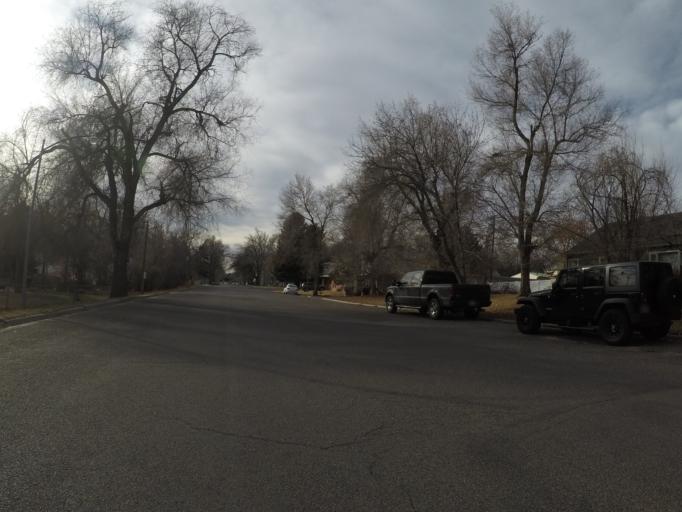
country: US
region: Montana
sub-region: Yellowstone County
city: Billings
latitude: 45.7958
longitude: -108.5123
